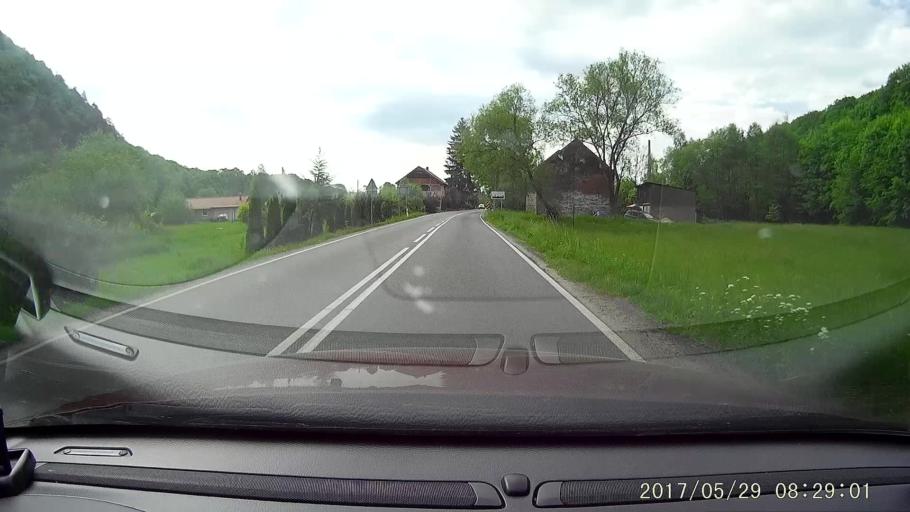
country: PL
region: Lower Silesian Voivodeship
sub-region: Powiat zlotoryjski
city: Swierzawa
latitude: 51.0358
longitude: 15.8661
